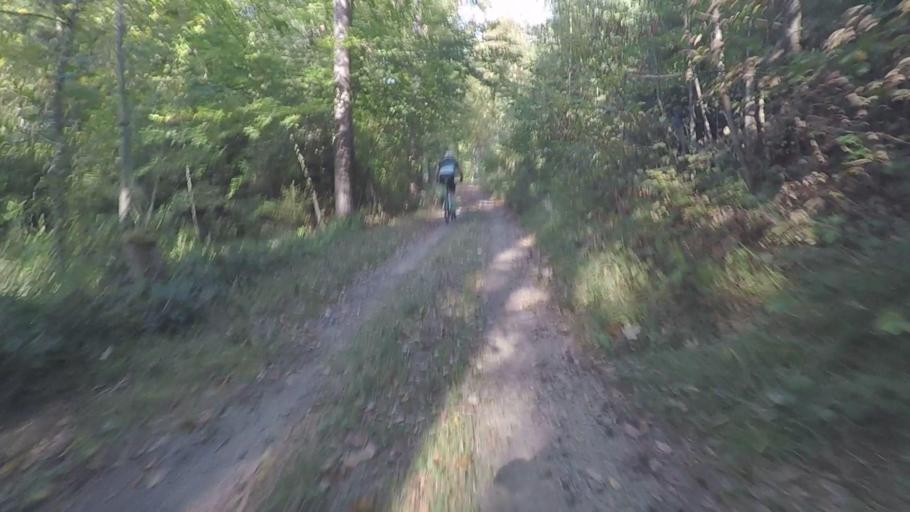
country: DE
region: Baden-Wuerttemberg
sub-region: Regierungsbezirk Stuttgart
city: Spiegelberg
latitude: 49.0395
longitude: 9.4803
